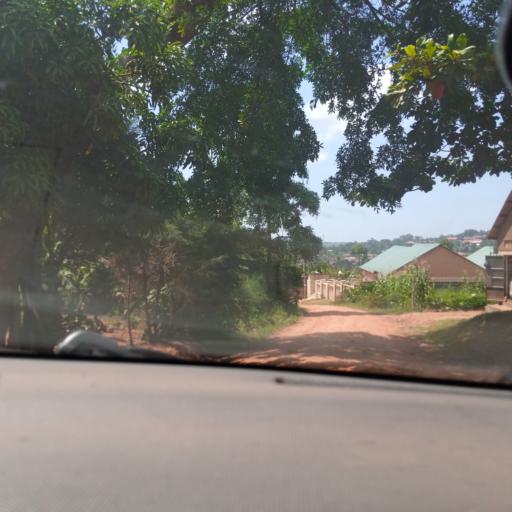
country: UG
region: Central Region
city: Masaka
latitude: -0.3231
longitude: 31.7450
